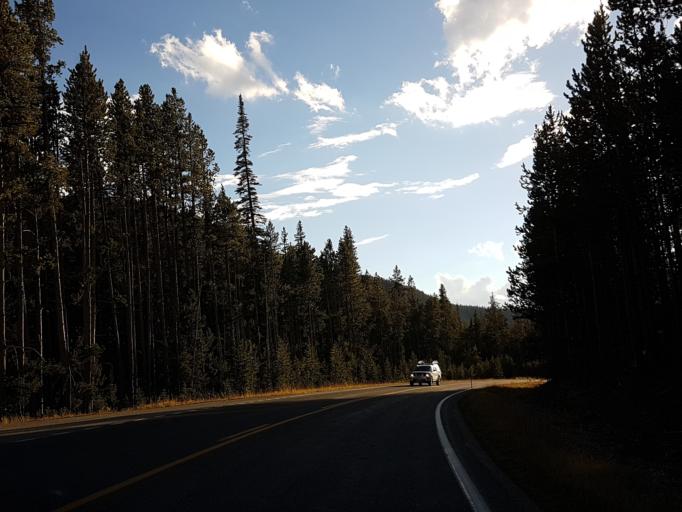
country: US
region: Montana
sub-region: Gallatin County
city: West Yellowstone
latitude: 44.4348
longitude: -110.7350
